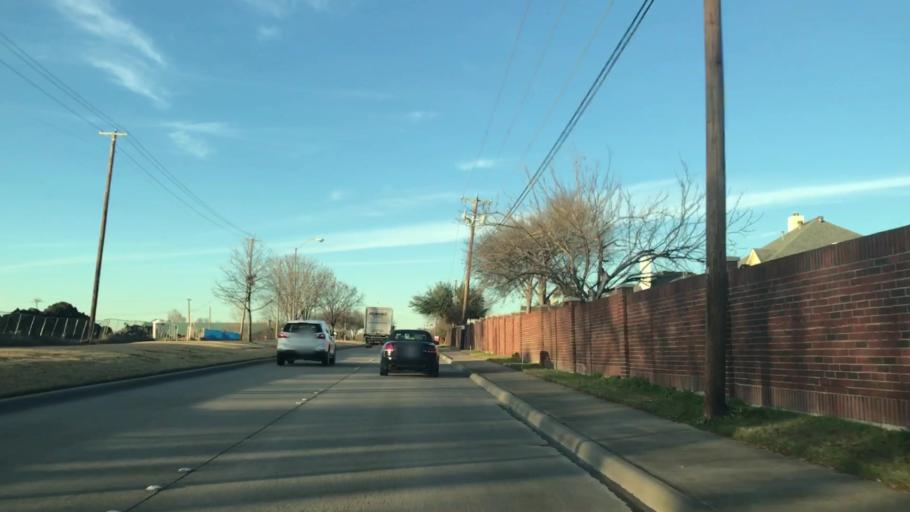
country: US
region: Texas
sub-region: Dallas County
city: Rowlett
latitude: 32.8979
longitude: -96.5181
